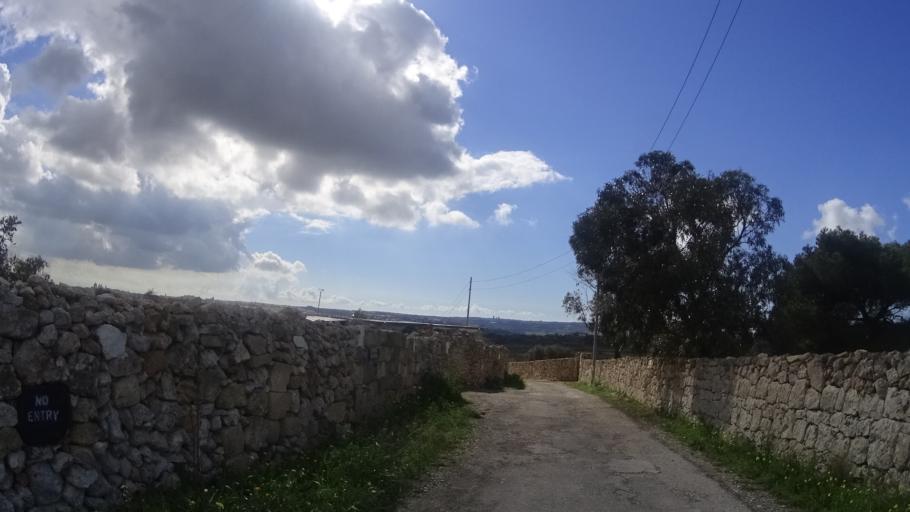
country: MT
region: L-Imtarfa
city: Imtarfa
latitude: 35.9058
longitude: 14.3841
